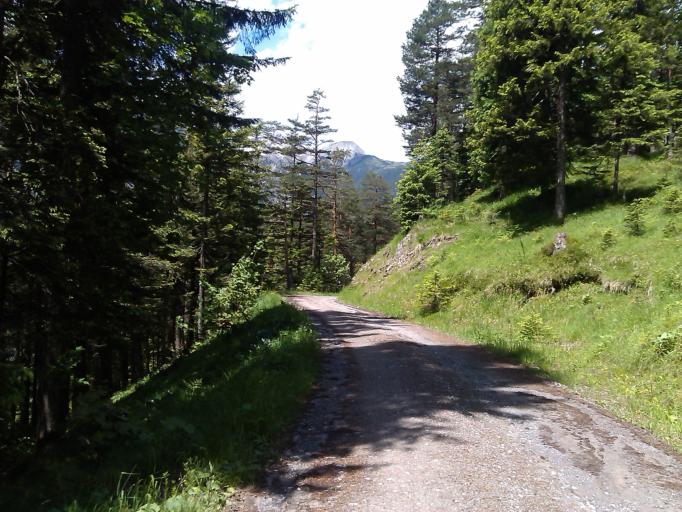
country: AT
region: Tyrol
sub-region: Politischer Bezirk Imst
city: Nassereith
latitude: 47.3540
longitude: 10.8452
